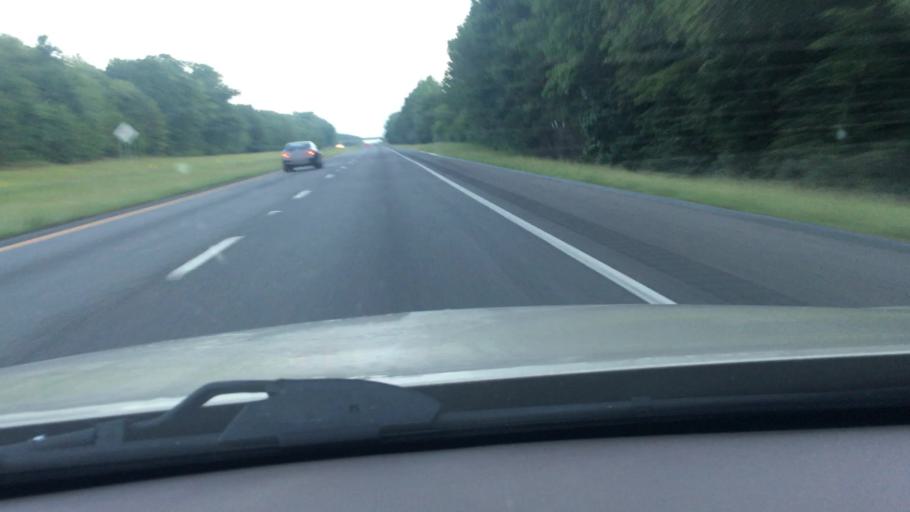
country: US
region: South Carolina
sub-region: Lexington County
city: Irmo
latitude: 34.1173
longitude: -81.1935
